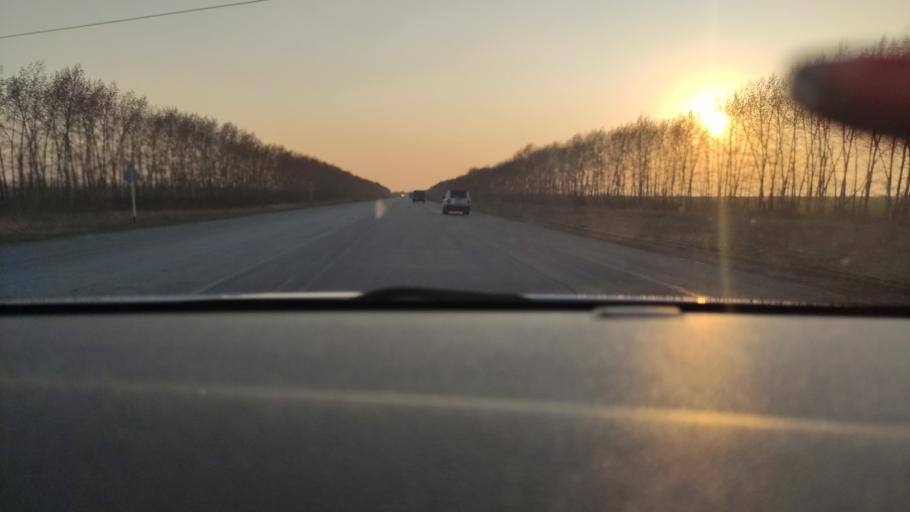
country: RU
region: Voronezj
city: Novovoronezh
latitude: 51.4173
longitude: 39.2765
